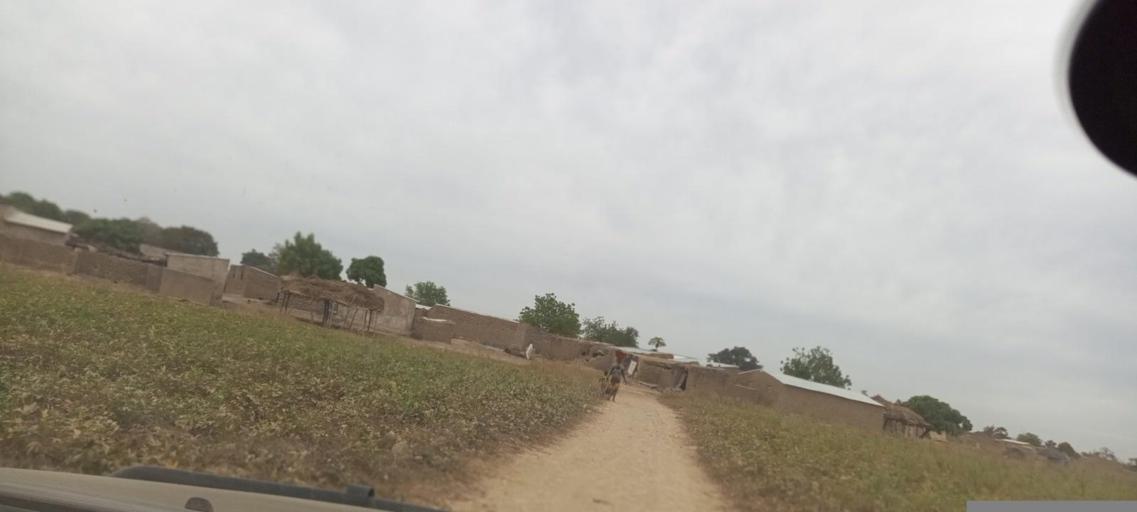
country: ML
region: Koulikoro
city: Kati
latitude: 12.7479
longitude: -8.3596
